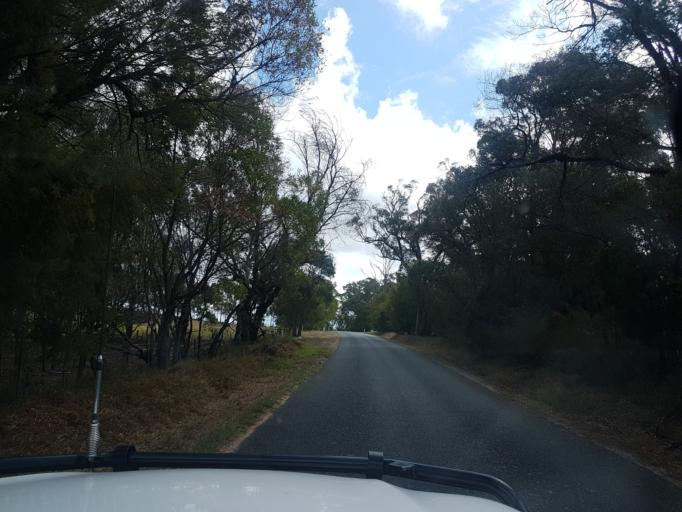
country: AU
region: Victoria
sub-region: East Gippsland
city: Bairnsdale
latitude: -37.7876
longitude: 147.5771
